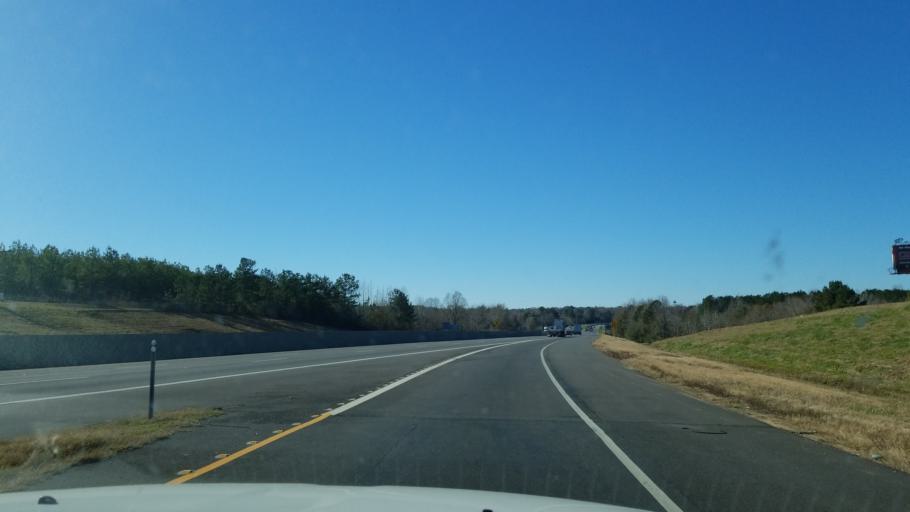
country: US
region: Alabama
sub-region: Tuscaloosa County
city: Holt
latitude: 33.1731
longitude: -87.4512
